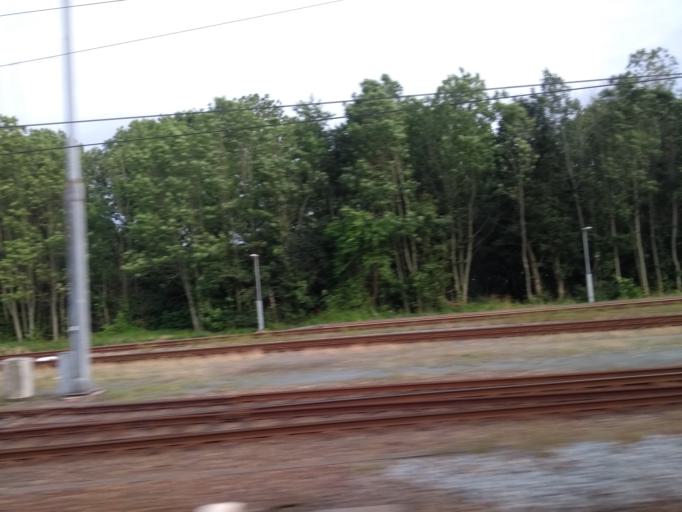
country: NL
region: Friesland
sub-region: Gemeente Leeuwarden
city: Bilgaard
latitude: 53.1947
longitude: 5.7811
